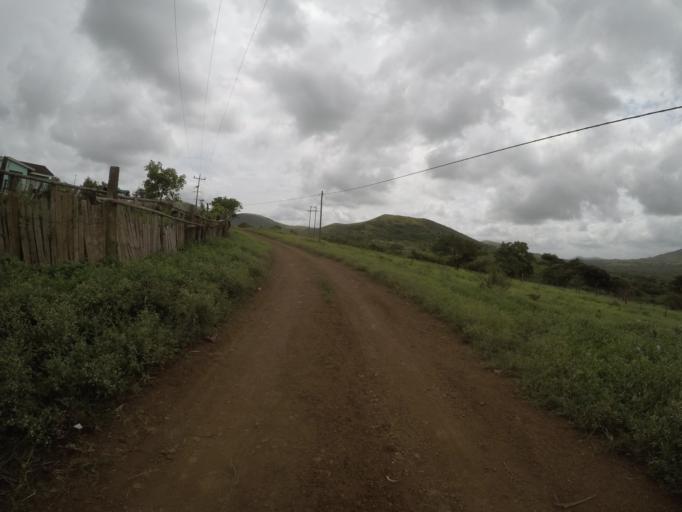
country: ZA
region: KwaZulu-Natal
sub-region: uThungulu District Municipality
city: Empangeni
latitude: -28.5894
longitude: 31.8887
